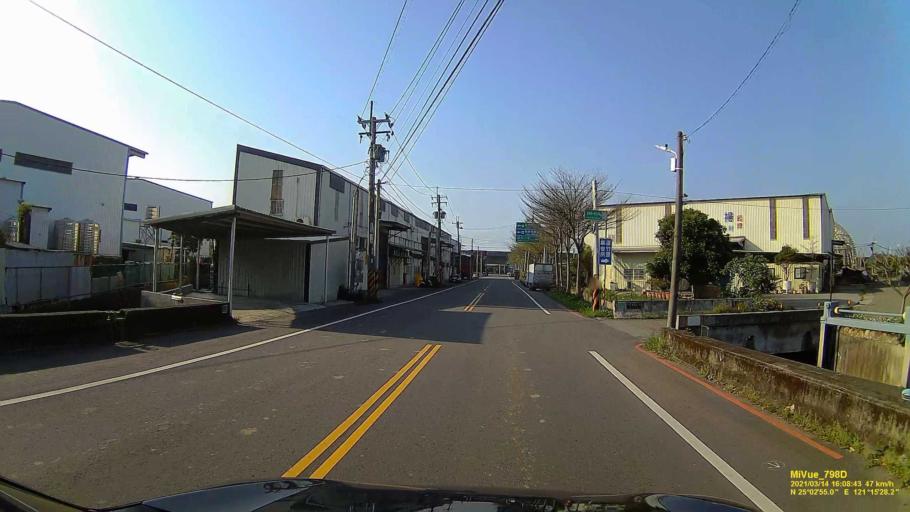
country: TW
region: Taiwan
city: Taoyuan City
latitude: 25.0488
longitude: 121.2577
